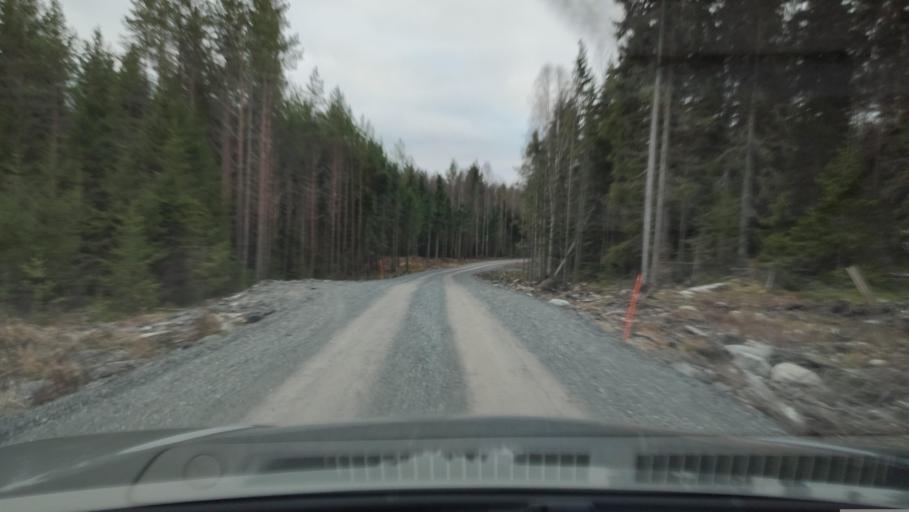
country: FI
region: Southern Ostrobothnia
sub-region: Suupohja
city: Karijoki
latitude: 62.1842
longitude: 21.5737
